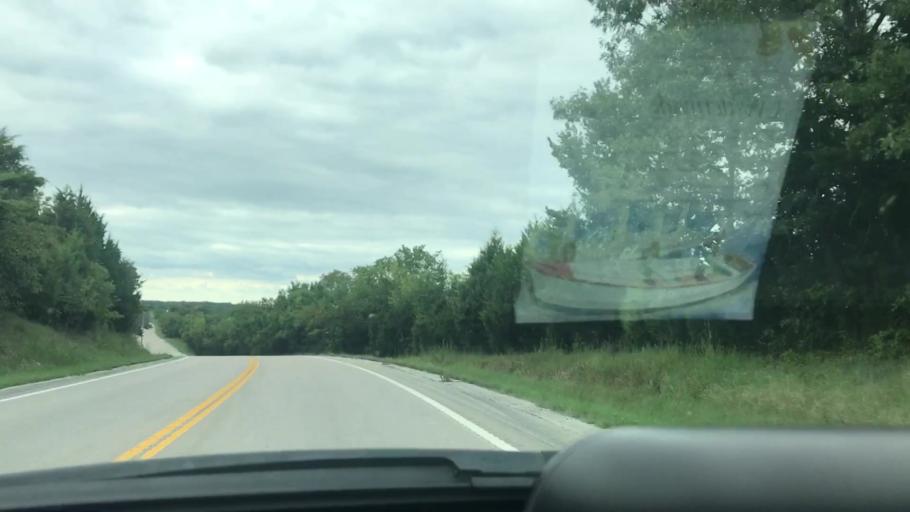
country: US
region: Missouri
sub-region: Benton County
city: Warsaw
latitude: 38.1699
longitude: -93.3108
